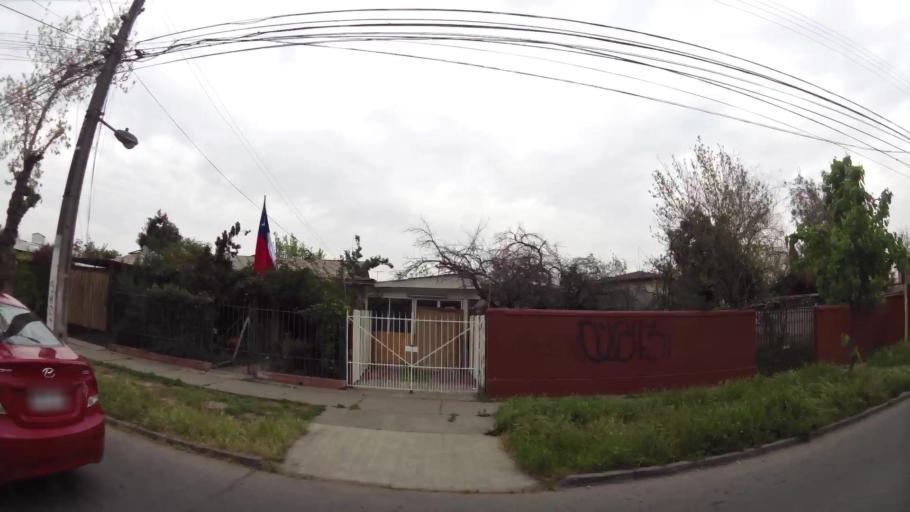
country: CL
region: Santiago Metropolitan
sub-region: Provincia de Santiago
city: Villa Presidente Frei, Nunoa, Santiago, Chile
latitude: -33.4943
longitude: -70.5917
